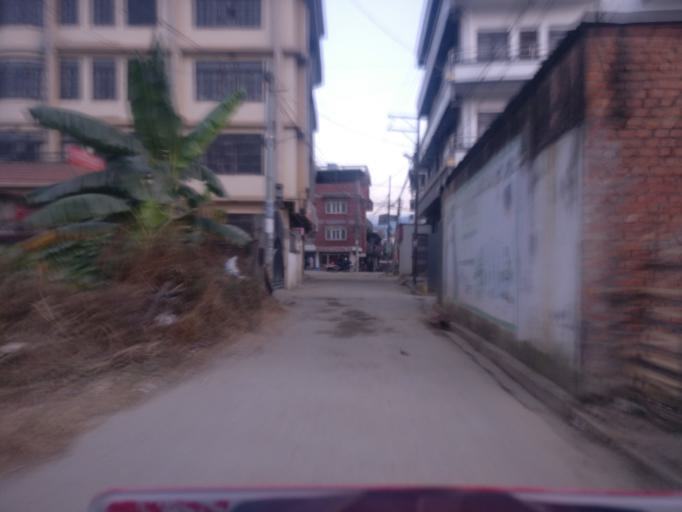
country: NP
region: Central Region
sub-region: Bagmati Zone
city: Patan
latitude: 27.6504
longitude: 85.3207
